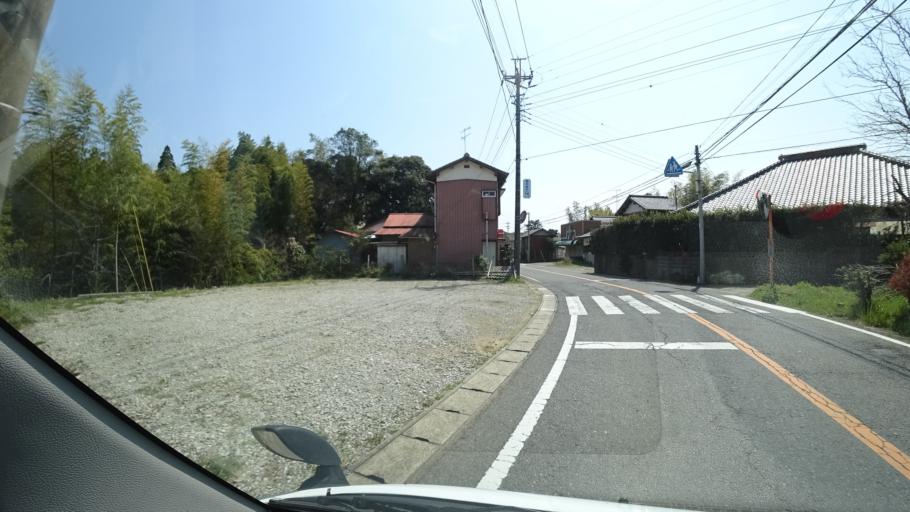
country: JP
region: Chiba
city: Naruto
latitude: 35.6920
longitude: 140.4164
